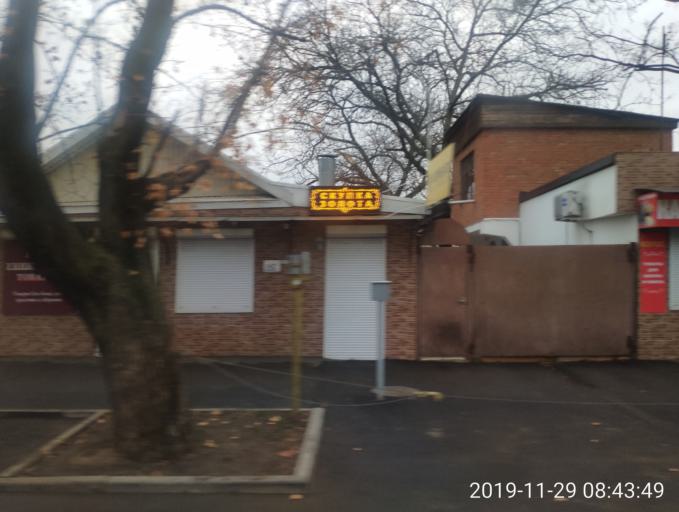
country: RU
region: Krasnodarskiy
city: Krasnodar
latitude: 45.0382
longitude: 38.9941
